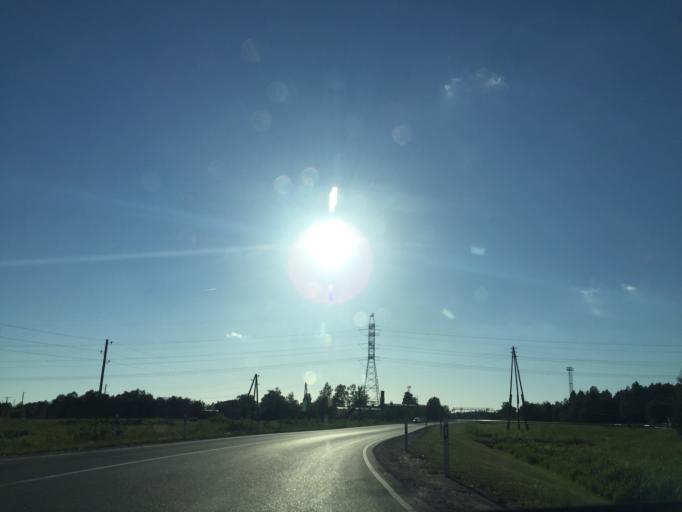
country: LV
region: Ventspils
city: Ventspils
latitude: 57.3928
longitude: 21.6370
